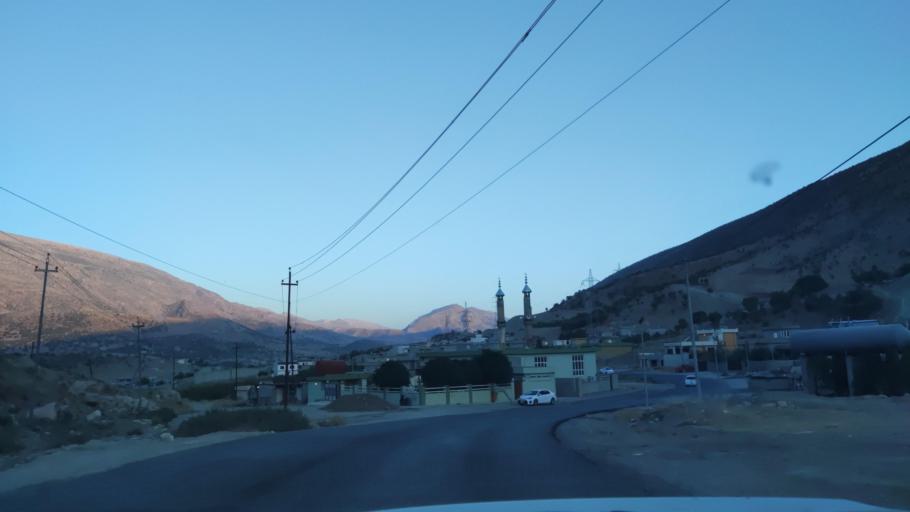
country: IQ
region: Arbil
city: Ruwandiz
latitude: 36.5924
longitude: 44.3855
